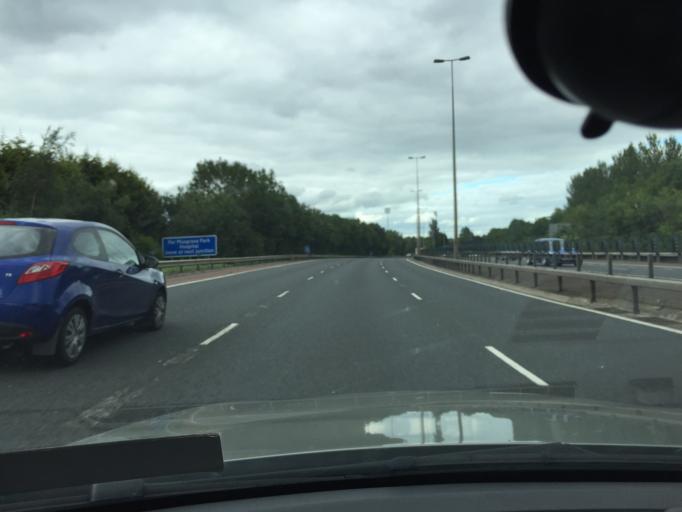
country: GB
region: Northern Ireland
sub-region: City of Belfast
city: Belfast
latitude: 54.5678
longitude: -5.9909
